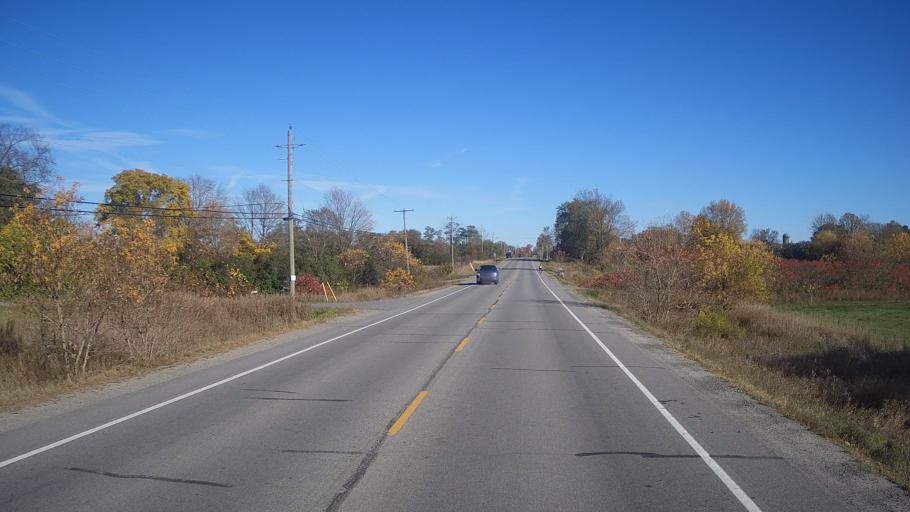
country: CA
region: Ontario
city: Kingston
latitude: 44.4073
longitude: -76.5684
